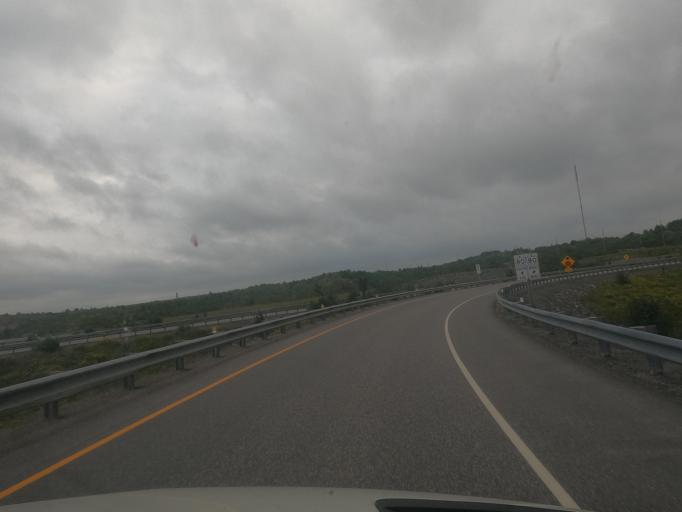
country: CA
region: Ontario
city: Greater Sudbury
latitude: 46.4299
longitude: -81.0066
